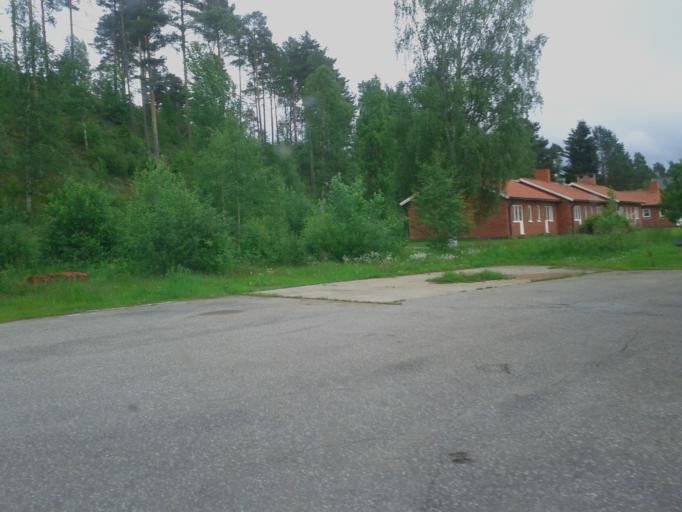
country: NO
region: Hedmark
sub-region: Trysil
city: Innbygda
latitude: 61.8581
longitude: 12.7147
